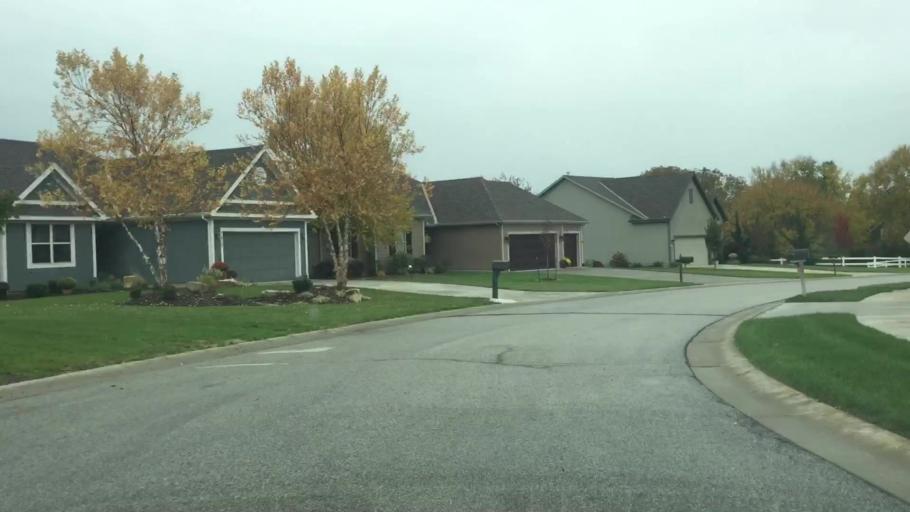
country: US
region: Kansas
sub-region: Wyandotte County
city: Edwardsville
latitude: 38.9974
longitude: -94.8251
